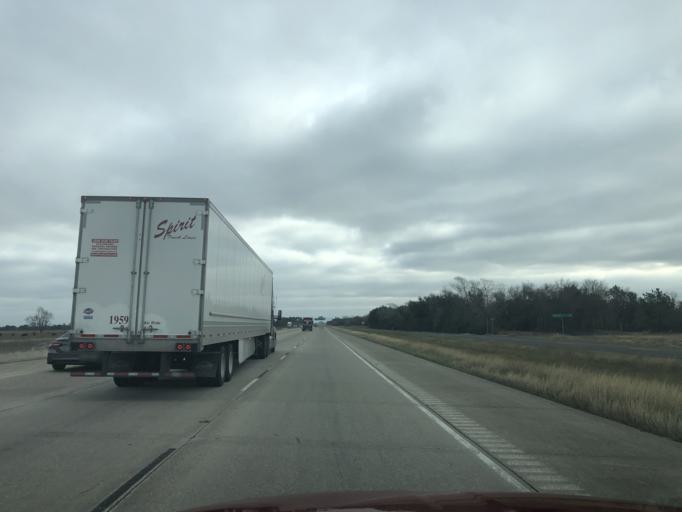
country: US
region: Texas
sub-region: Chambers County
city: Winnie
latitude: 29.8269
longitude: -94.4298
